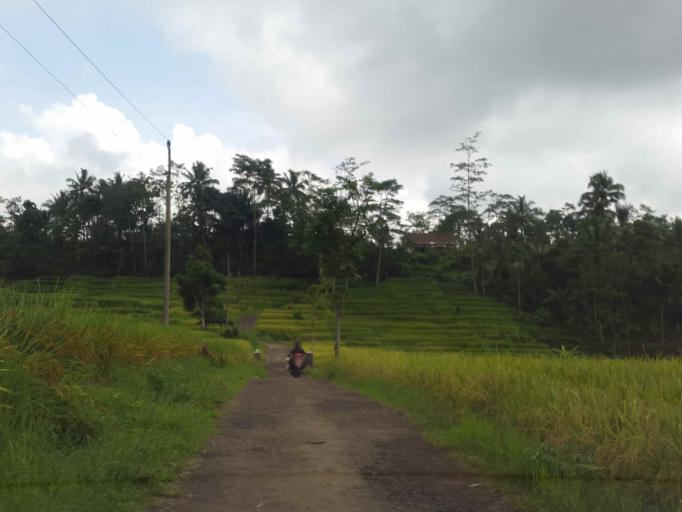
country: ID
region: Central Java
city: Cigintung
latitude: -7.2363
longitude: 108.6981
